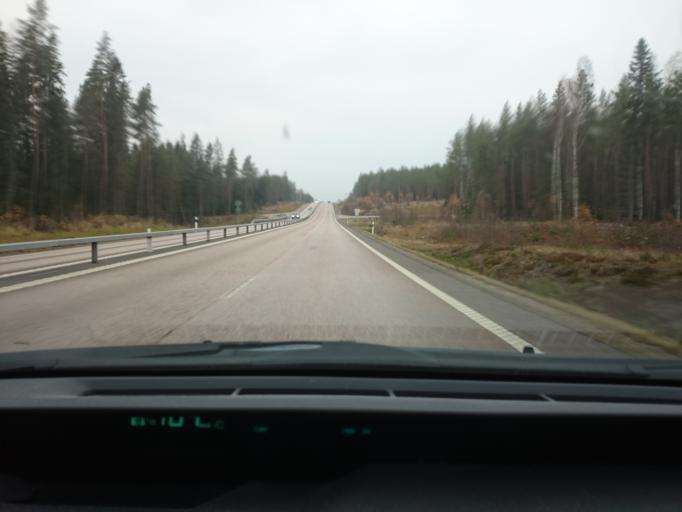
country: SE
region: Vaestmanland
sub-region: Sala Kommun
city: Sala
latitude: 60.0081
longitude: 16.3995
